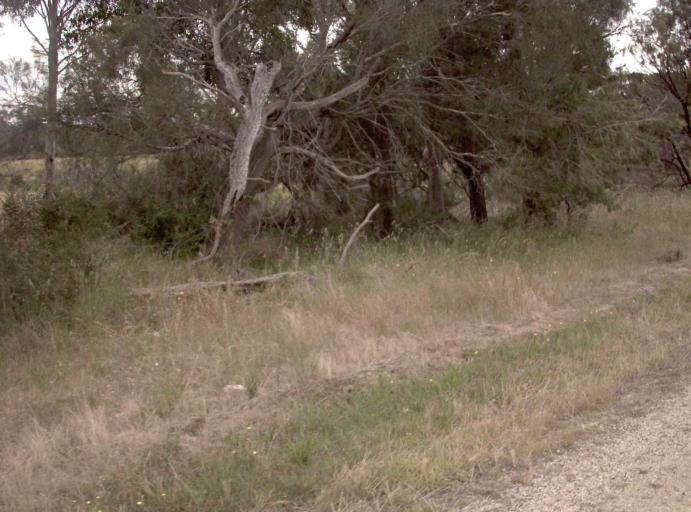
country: AU
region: Victoria
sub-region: Wellington
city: Sale
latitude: -38.1798
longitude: 147.1444
